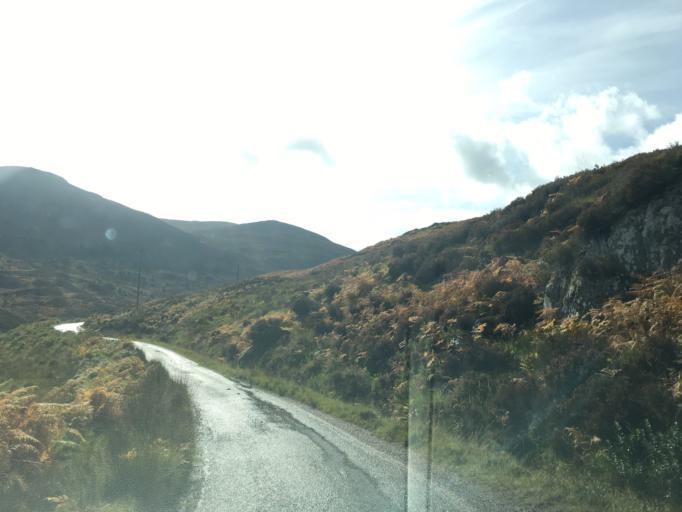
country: GB
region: Scotland
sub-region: Highland
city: Spean Bridge
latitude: 57.3454
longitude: -4.9322
